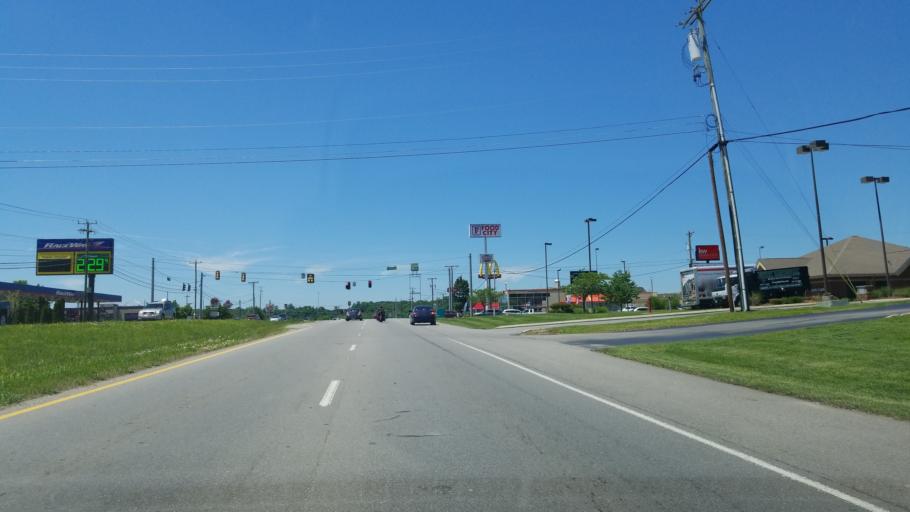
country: US
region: Tennessee
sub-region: Hamilton County
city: Collegedale
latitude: 35.0836
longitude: -85.0606
